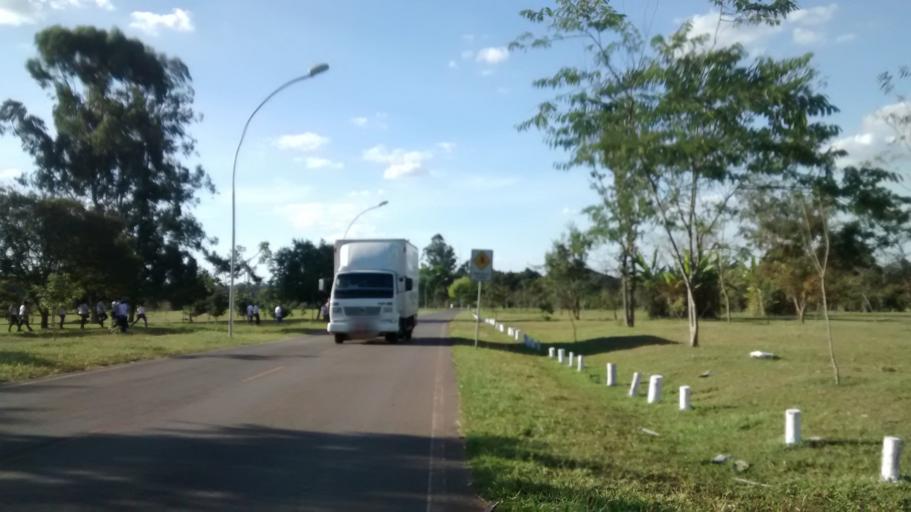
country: BR
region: Federal District
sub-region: Brasilia
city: Brasilia
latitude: -15.8353
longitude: -48.0246
